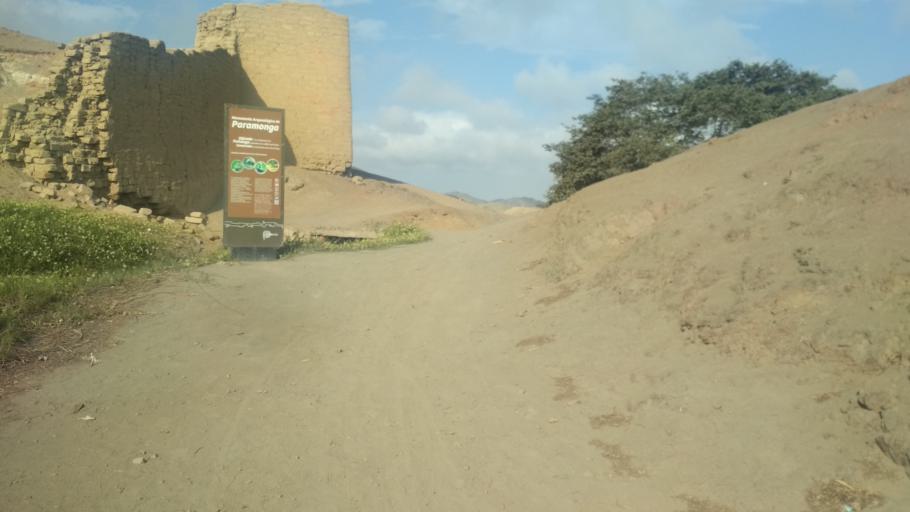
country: PE
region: Lima
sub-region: Barranca
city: Paramonga
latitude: -10.6539
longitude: -77.8408
